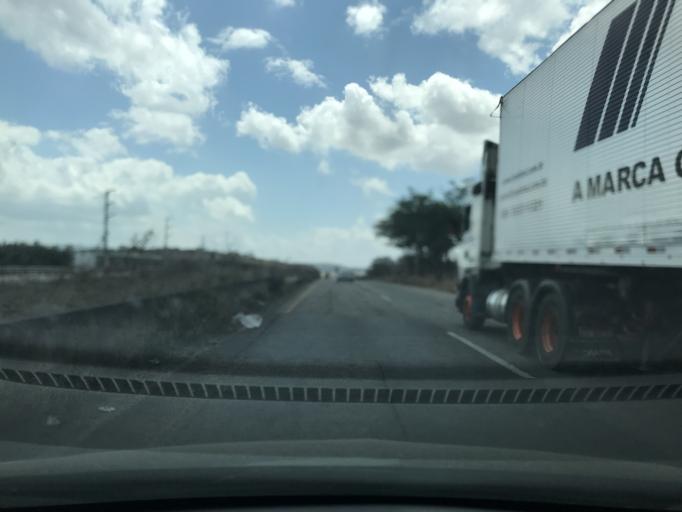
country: BR
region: Pernambuco
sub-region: Caruaru
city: Caruaru
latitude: -8.3047
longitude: -35.9307
